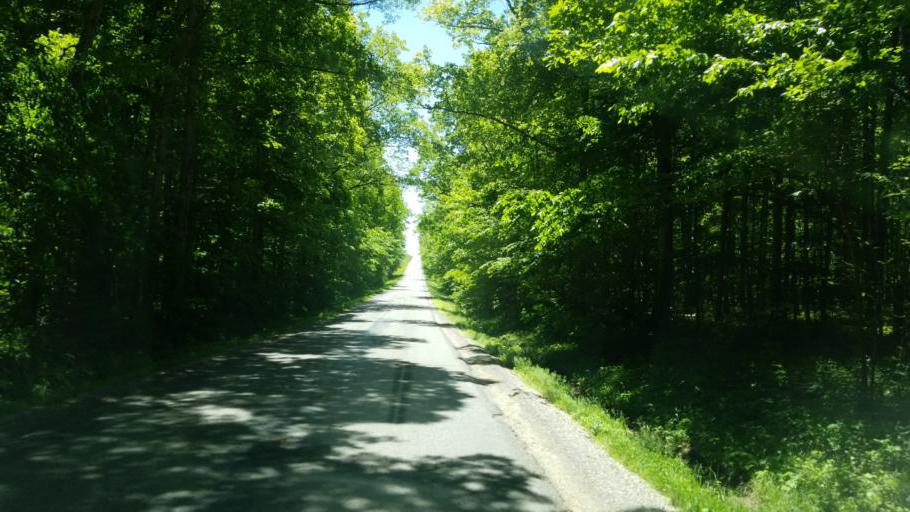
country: US
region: Ohio
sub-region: Mercer County
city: Fort Recovery
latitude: 40.3229
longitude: -84.8036
